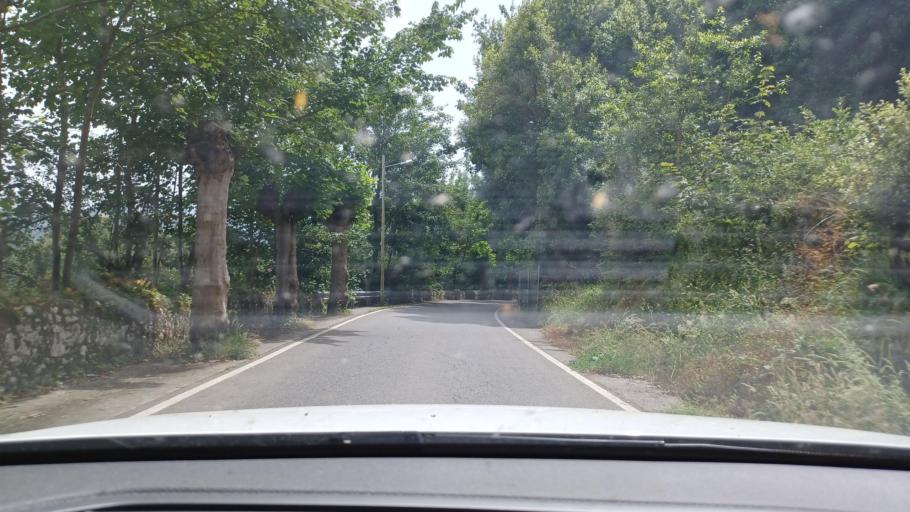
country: ES
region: Asturias
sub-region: Province of Asturias
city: Llanes
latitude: 43.4175
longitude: -4.7564
